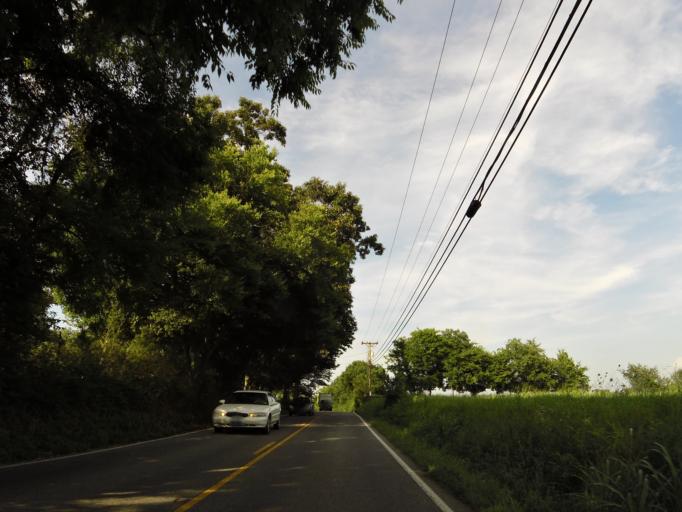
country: US
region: Tennessee
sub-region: Blount County
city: Wildwood
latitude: 35.8050
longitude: -83.8448
